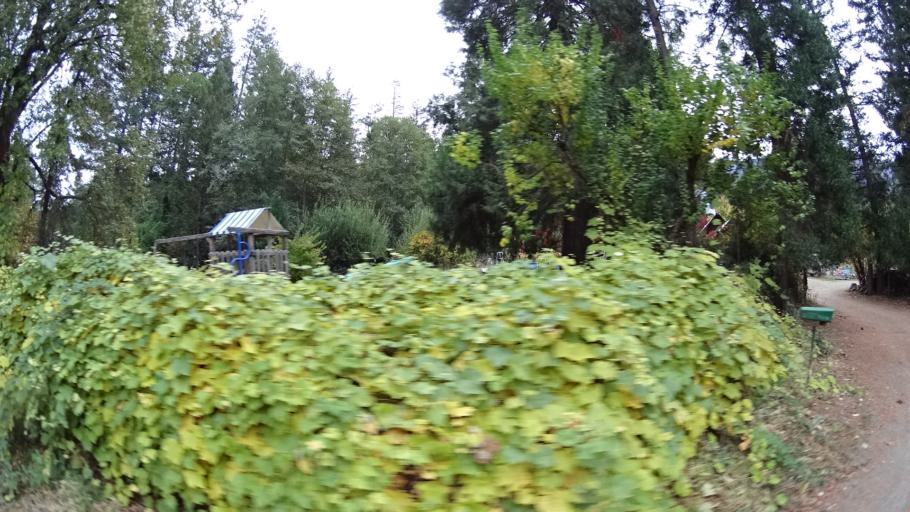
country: US
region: California
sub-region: Siskiyou County
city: Happy Camp
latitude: 41.8349
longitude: -123.1738
